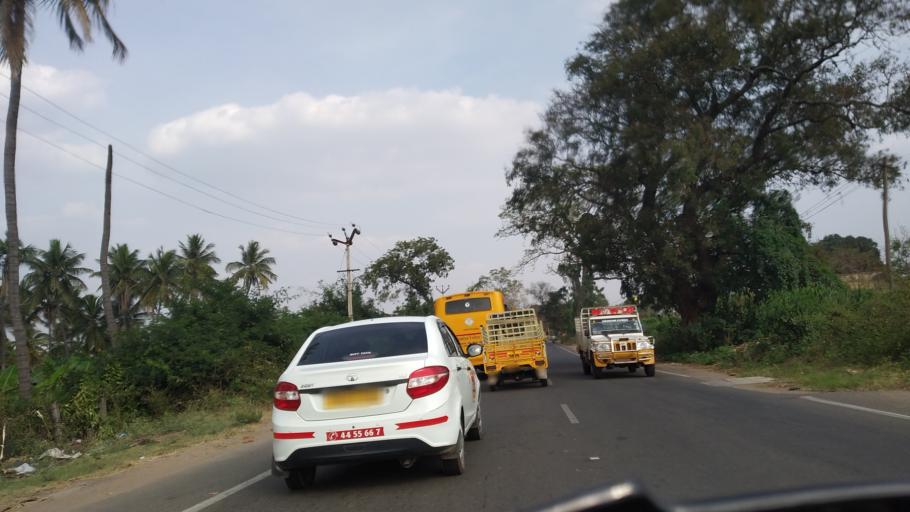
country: IN
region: Tamil Nadu
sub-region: Coimbatore
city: Perur
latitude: 10.9728
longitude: 76.8771
